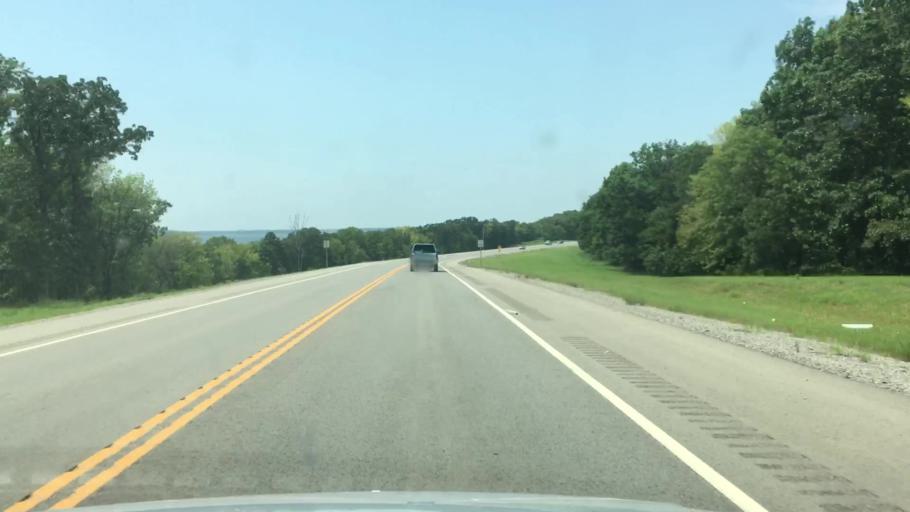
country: US
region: Oklahoma
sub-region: Wagoner County
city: Wagoner
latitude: 35.9288
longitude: -95.2567
